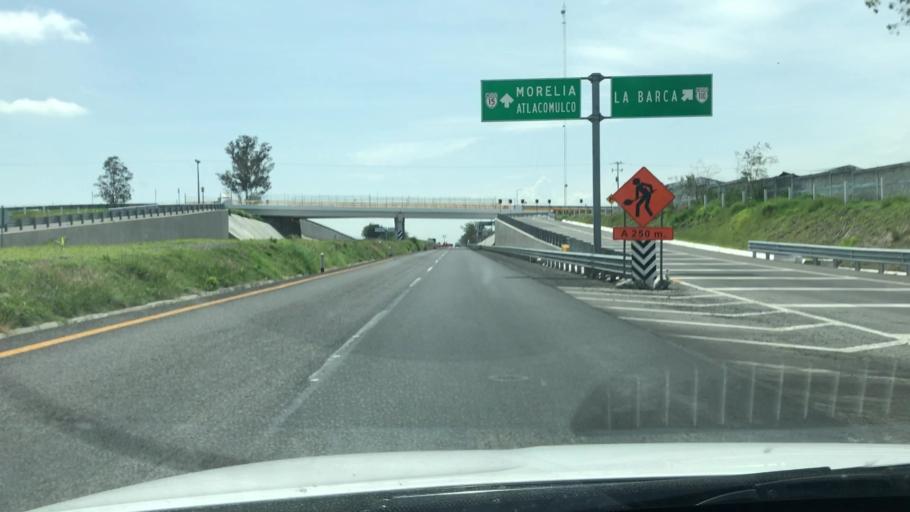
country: MX
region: Jalisco
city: La Barca
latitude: 20.3229
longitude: -102.5694
